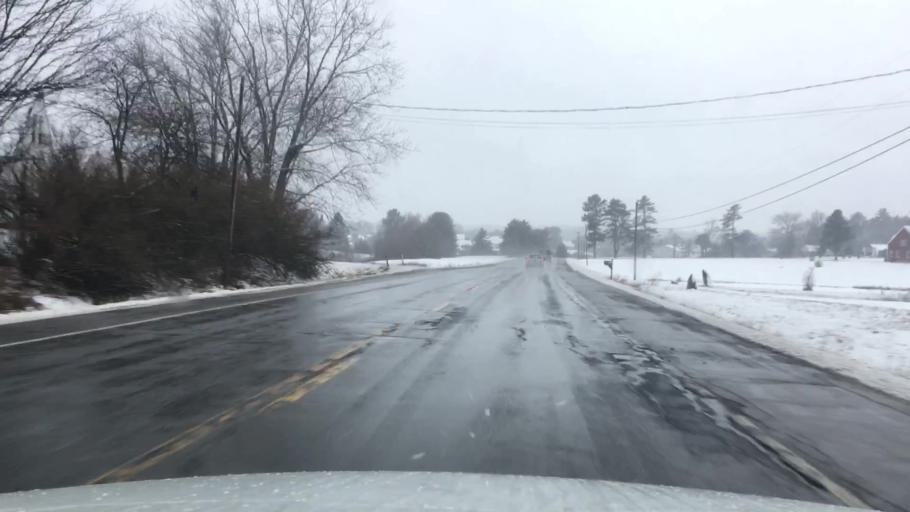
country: US
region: Maine
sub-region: Knox County
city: Warren
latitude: 44.1287
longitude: -69.2297
